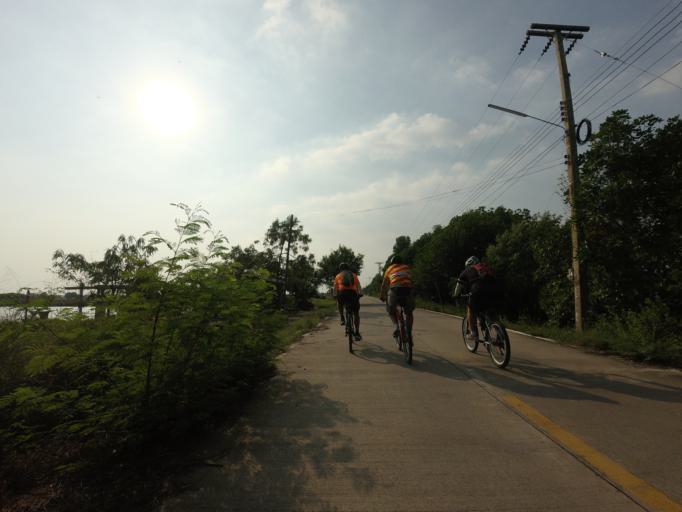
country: TH
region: Samut Sakhon
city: Samut Sakhon
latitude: 13.5080
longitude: 100.3227
